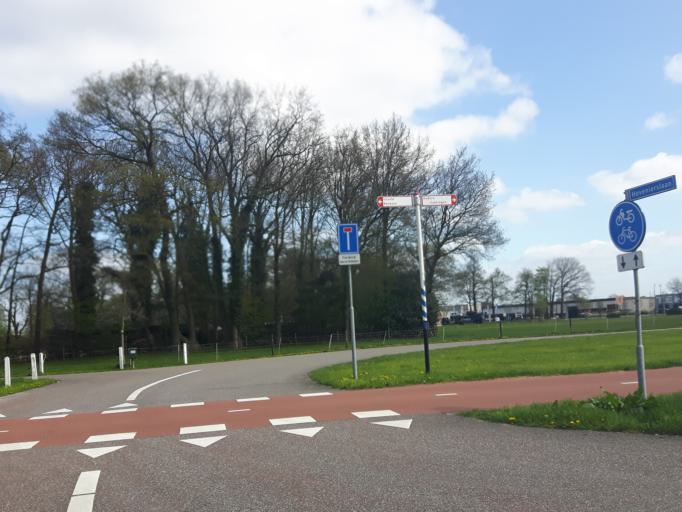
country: NL
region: Overijssel
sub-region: Gemeente Hengelo
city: Hengelo
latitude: 52.2178
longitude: 6.8325
